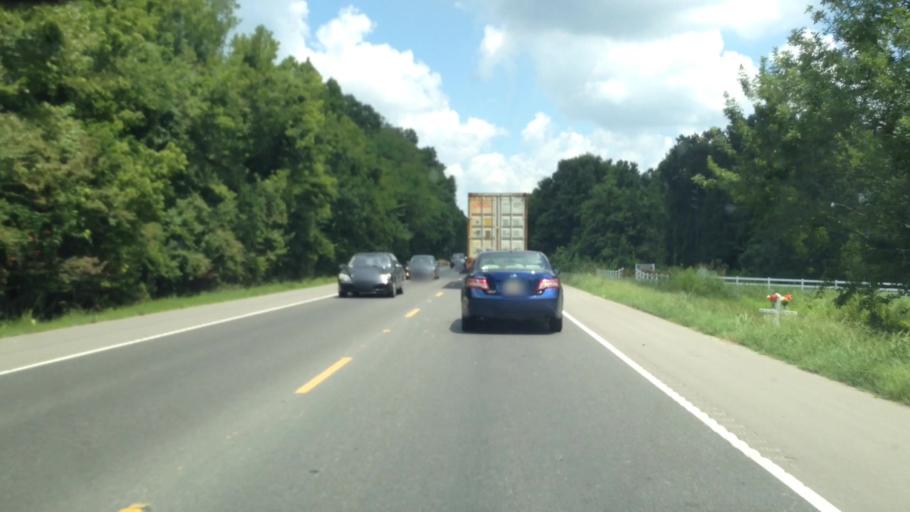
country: US
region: Louisiana
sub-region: Ascension Parish
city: Sorrento
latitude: 30.1595
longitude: -90.8778
